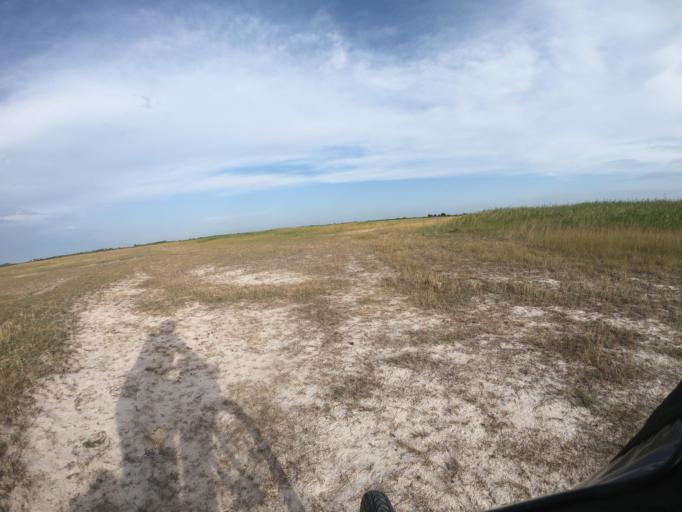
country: HU
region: Hajdu-Bihar
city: Hortobagy
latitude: 47.6016
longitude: 21.0611
